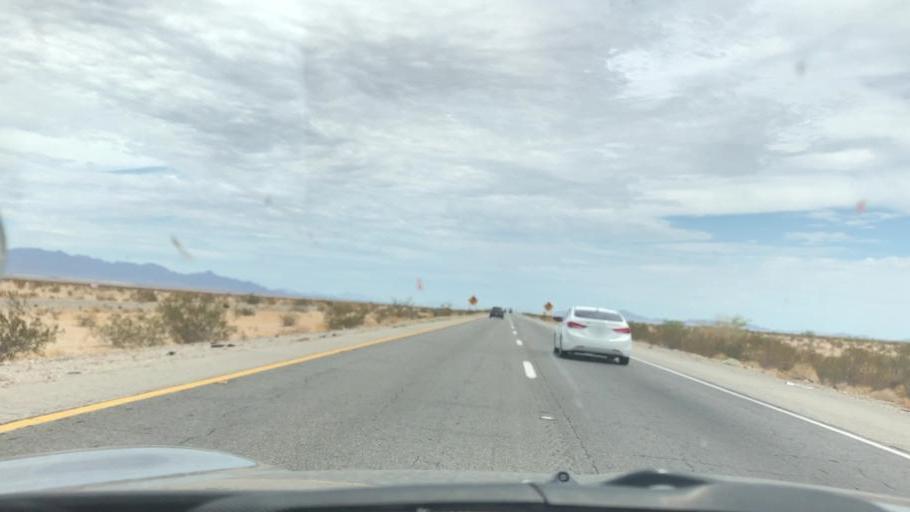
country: US
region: California
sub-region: Riverside County
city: Mesa Verde
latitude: 33.6410
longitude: -115.1025
